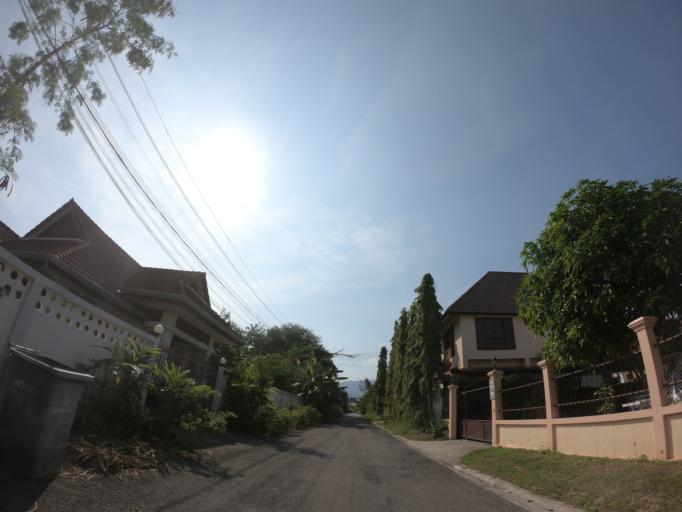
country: TH
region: Chiang Mai
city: Chiang Mai
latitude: 18.8228
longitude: 98.9882
